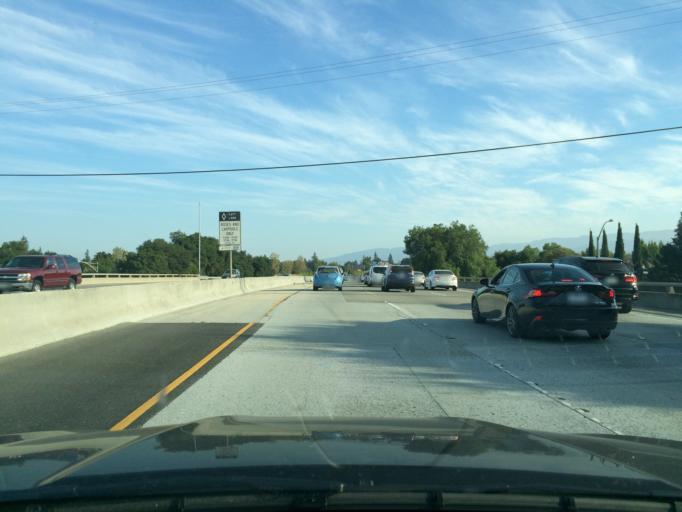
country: US
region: California
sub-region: Santa Clara County
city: Sunnyvale
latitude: 37.3528
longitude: -122.0609
